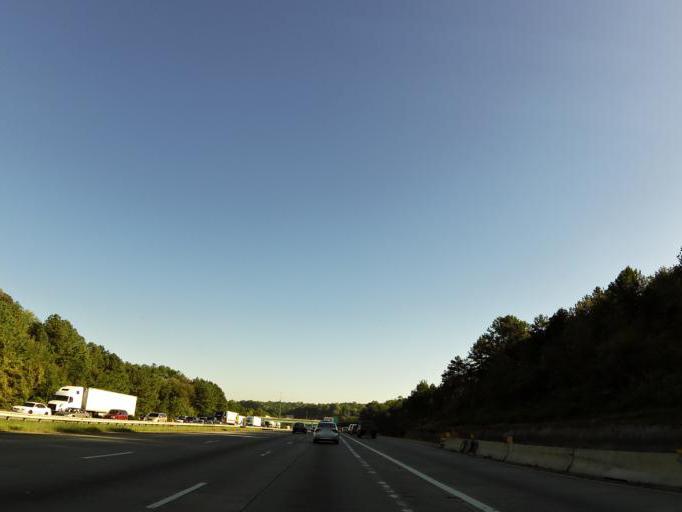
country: US
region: Georgia
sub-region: Cobb County
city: Marietta
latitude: 34.0034
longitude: -84.5642
